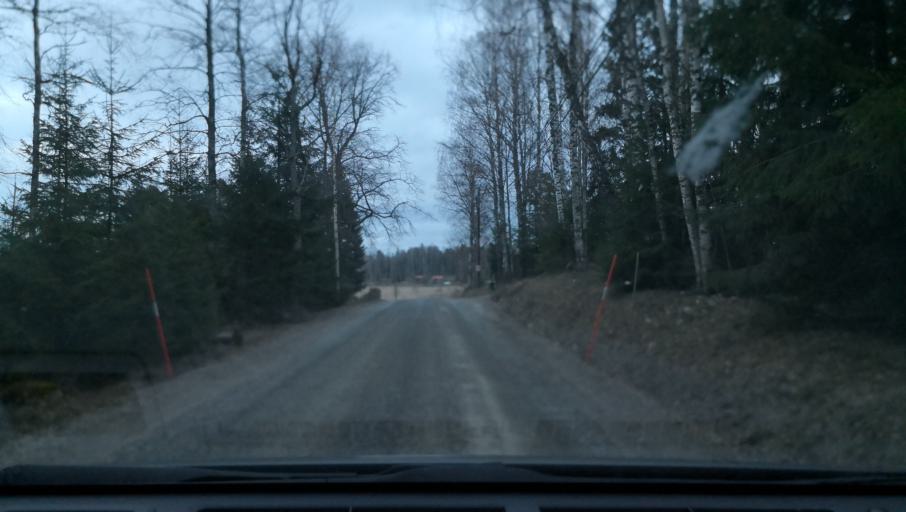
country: SE
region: Vaestmanland
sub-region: Kopings Kommun
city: Kolsva
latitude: 59.5876
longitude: 15.7148
